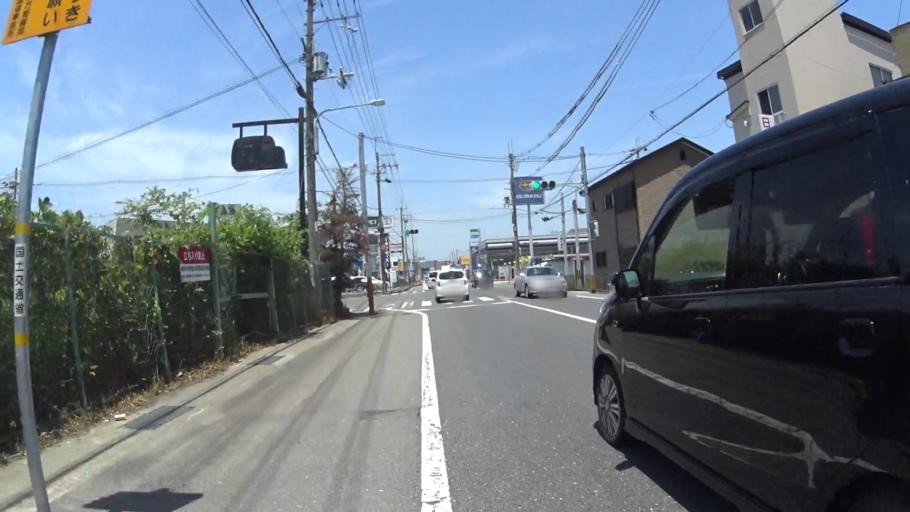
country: JP
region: Kyoto
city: Kameoka
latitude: 35.0269
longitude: 135.5561
